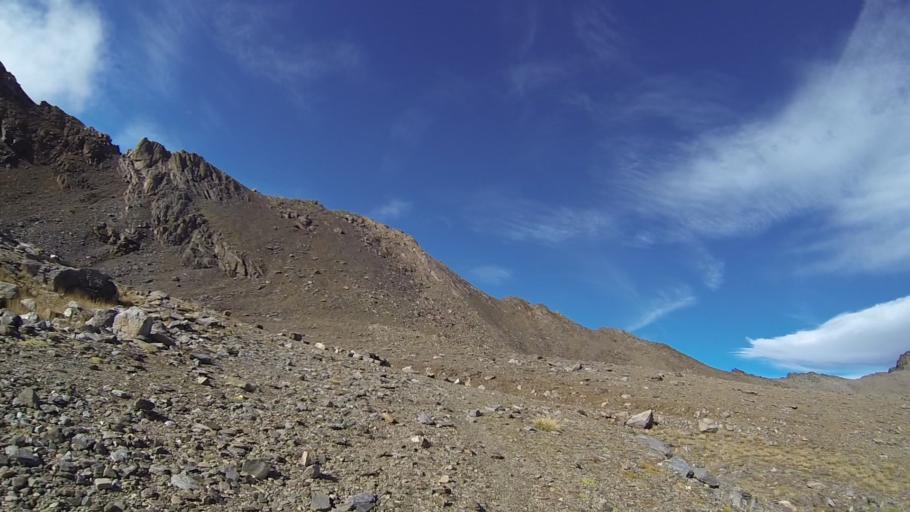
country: ES
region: Andalusia
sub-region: Provincia de Granada
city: Trevelez
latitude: 37.0537
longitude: -3.3274
